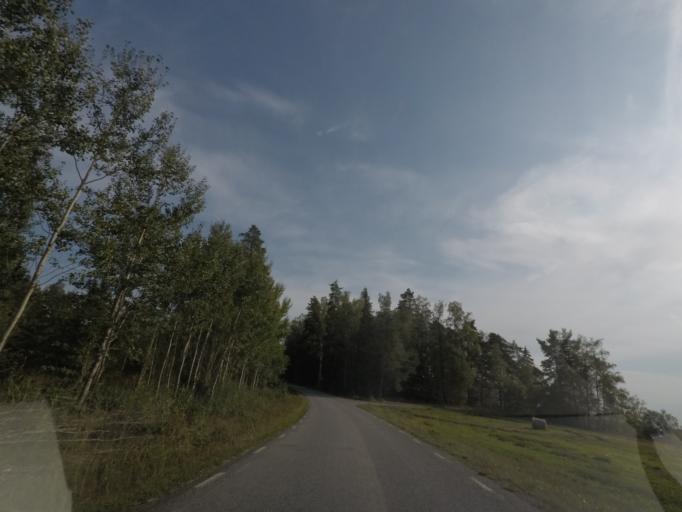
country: SE
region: Vaestmanland
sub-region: Kungsors Kommun
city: Kungsoer
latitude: 59.5117
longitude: 16.1498
